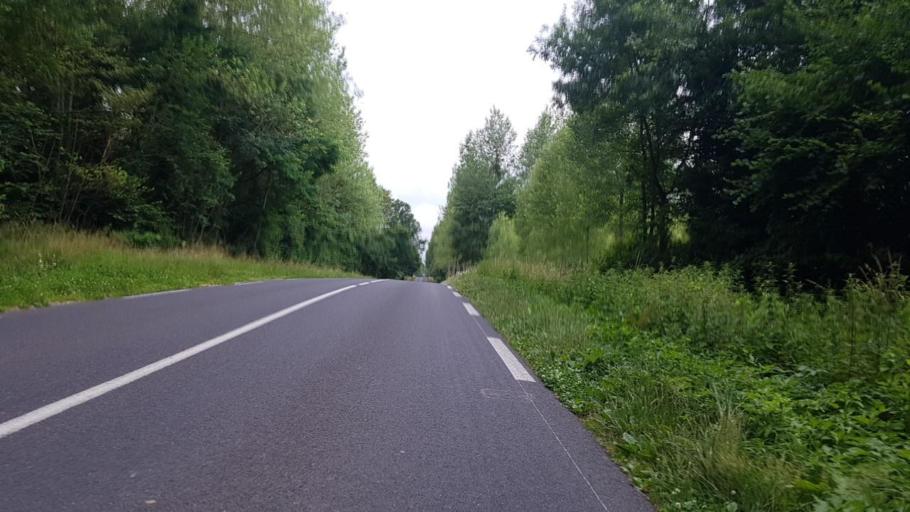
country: FR
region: Champagne-Ardenne
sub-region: Departement de la Marne
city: Sermaize-les-Bains
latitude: 48.7784
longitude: 4.8917
